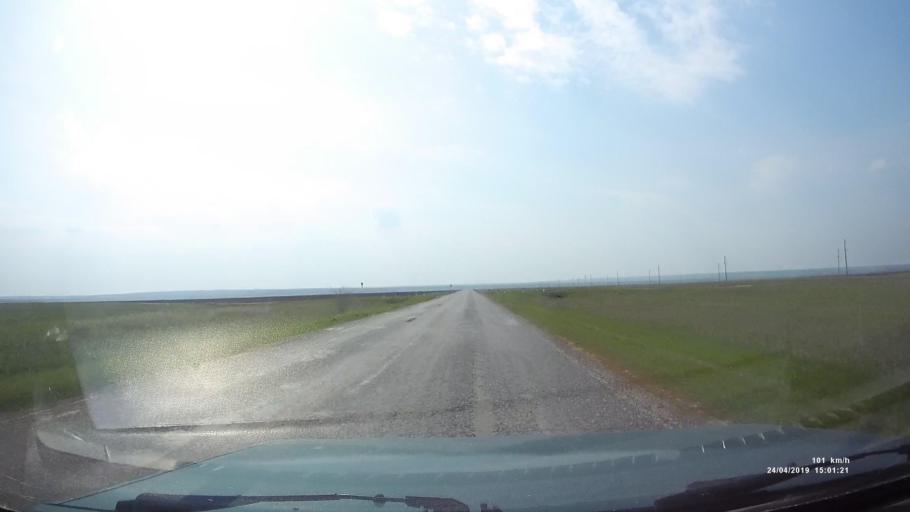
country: RU
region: Rostov
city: Remontnoye
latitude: 46.5659
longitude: 43.5356
